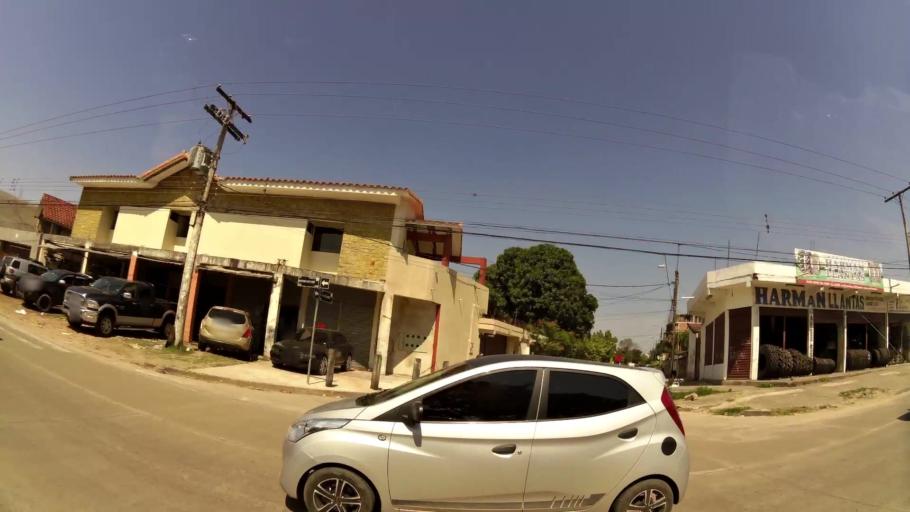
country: BO
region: Santa Cruz
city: Santa Cruz de la Sierra
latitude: -17.7513
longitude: -63.1893
